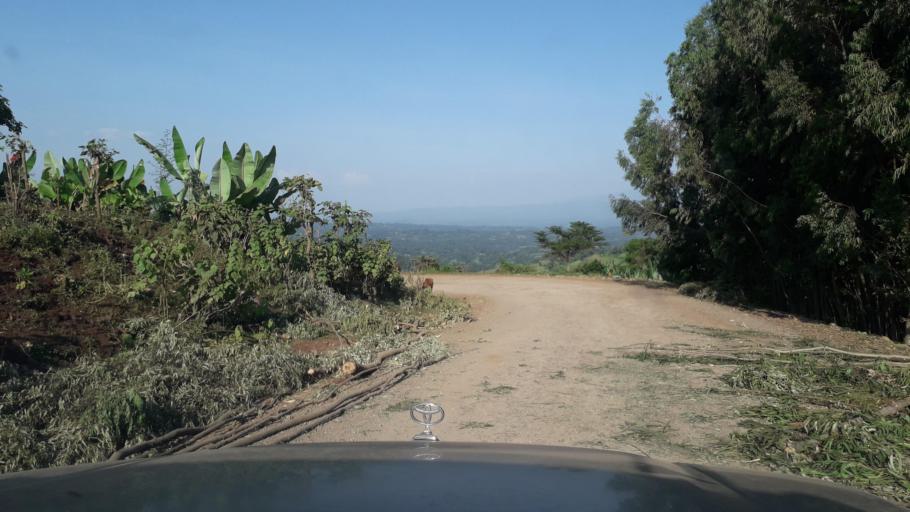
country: ET
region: Oromiya
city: Jima
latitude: 7.4713
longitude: 36.8781
